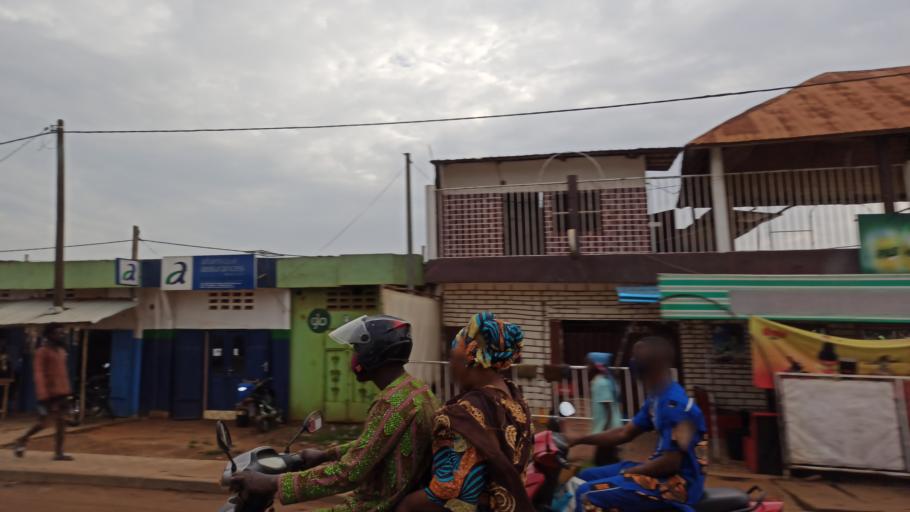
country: BJ
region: Queme
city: Porto-Novo
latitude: 6.5195
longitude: 2.6030
